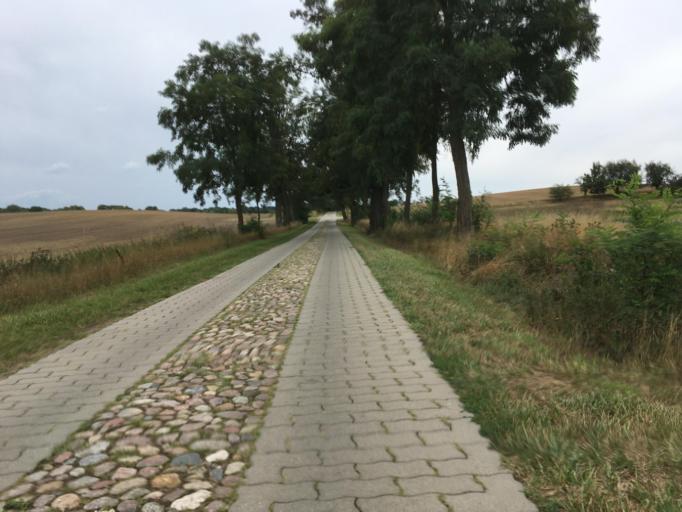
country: DE
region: Brandenburg
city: Passow
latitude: 53.0983
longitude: 14.1183
